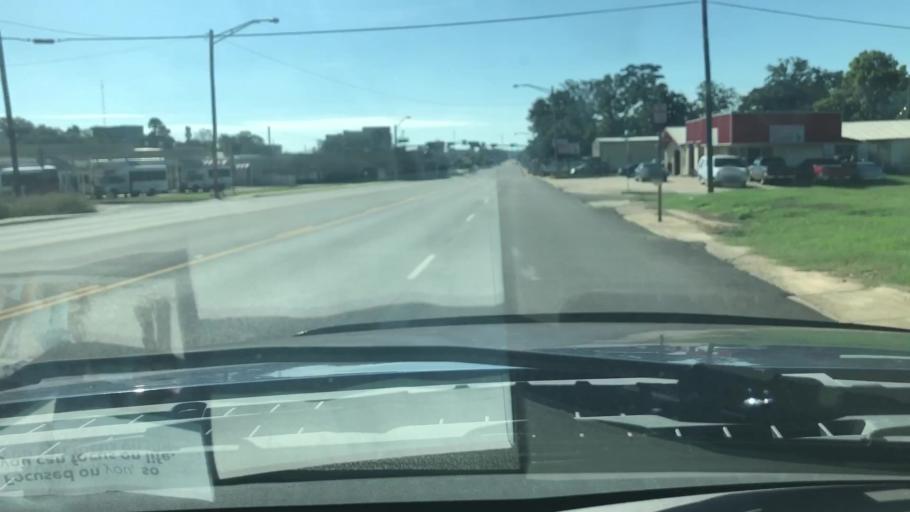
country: US
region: Texas
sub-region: Bowie County
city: Texarkana
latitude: 33.4326
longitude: -94.0526
